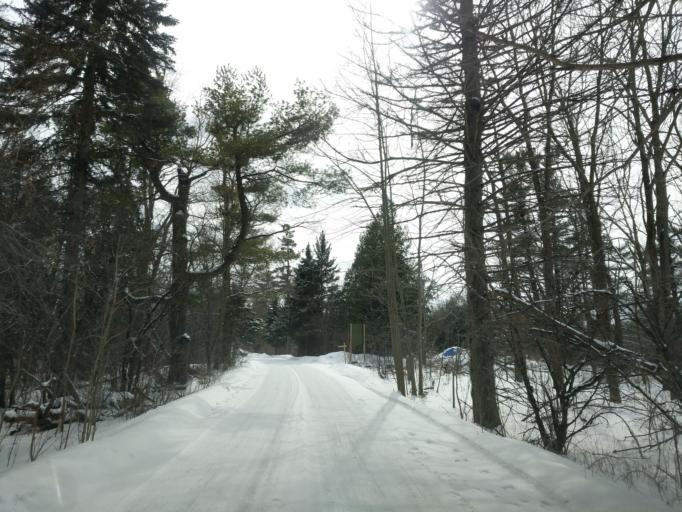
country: CA
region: Ontario
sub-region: York
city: Richmond Hill
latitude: 43.9535
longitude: -79.4235
